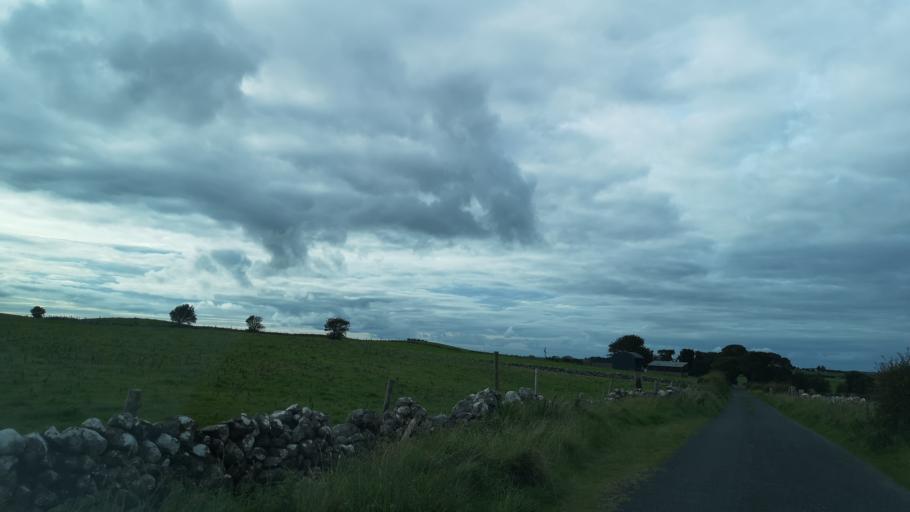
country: IE
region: Connaught
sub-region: County Galway
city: Ballinasloe
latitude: 53.3716
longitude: -8.1648
